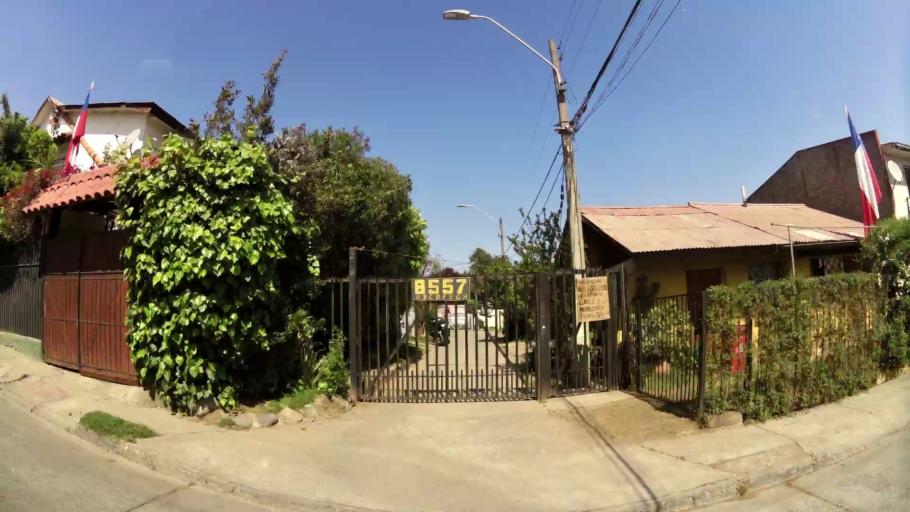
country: CL
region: Santiago Metropolitan
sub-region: Provincia de Santiago
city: Villa Presidente Frei, Nunoa, Santiago, Chile
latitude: -33.4659
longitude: -70.5411
